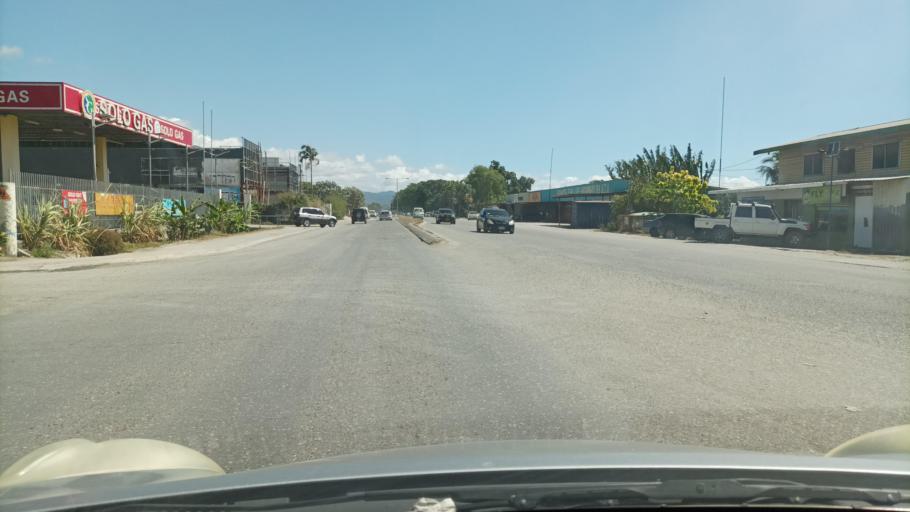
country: SB
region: Guadalcanal
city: Honiara
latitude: -9.4305
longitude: 159.9975
